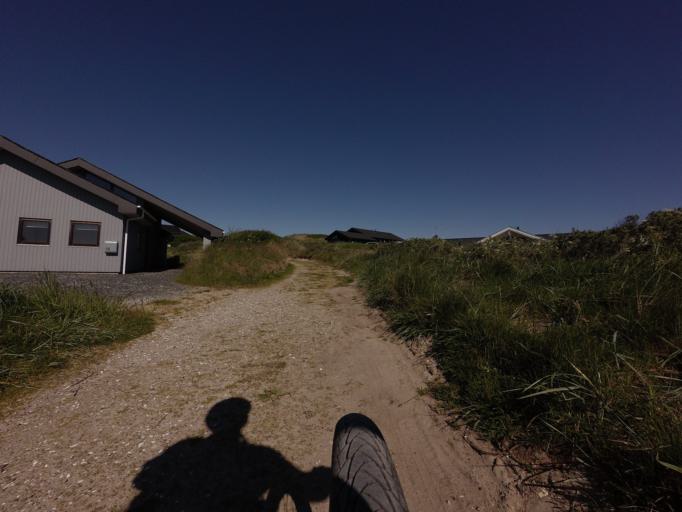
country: DK
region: North Denmark
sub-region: Jammerbugt Kommune
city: Pandrup
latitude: 57.3358
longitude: 9.6755
